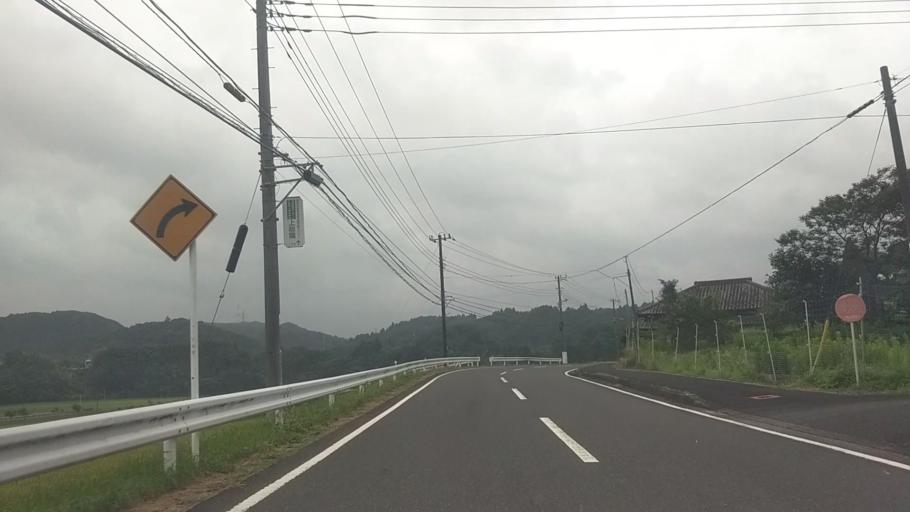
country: JP
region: Chiba
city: Kawaguchi
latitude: 35.2588
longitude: 140.0551
